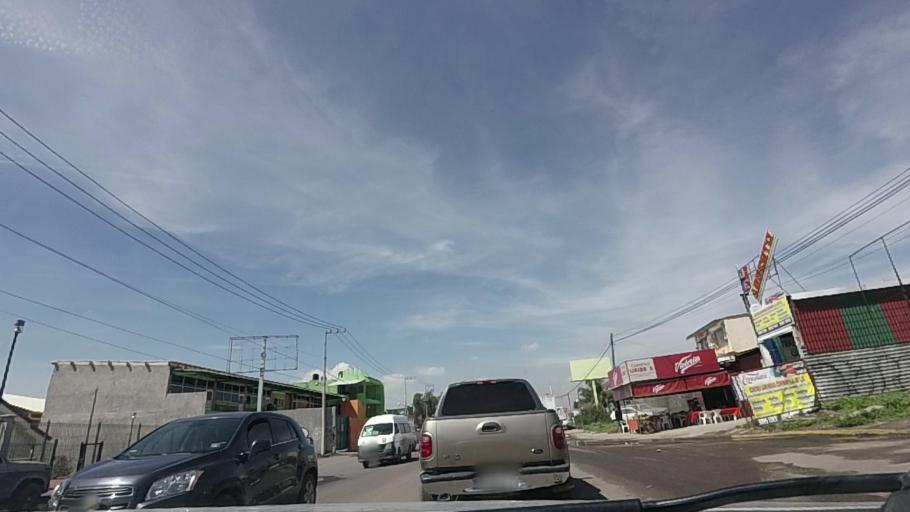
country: MX
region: Mexico
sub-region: Cuautitlan
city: Barrio Tlatenco
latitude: 19.7280
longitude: -99.1872
